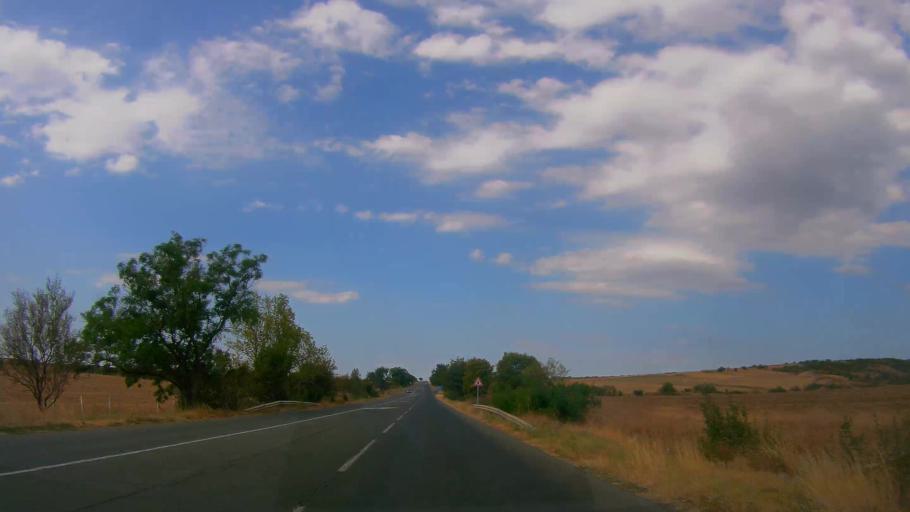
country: BG
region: Burgas
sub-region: Obshtina Aytos
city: Aytos
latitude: 42.6967
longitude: 27.1944
